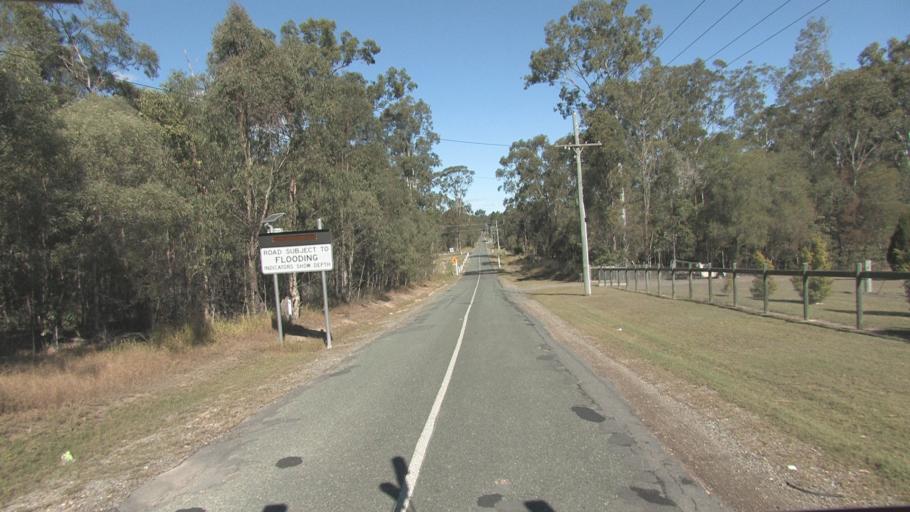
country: AU
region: Queensland
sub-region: Logan
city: Chambers Flat
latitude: -27.7967
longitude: 153.0705
